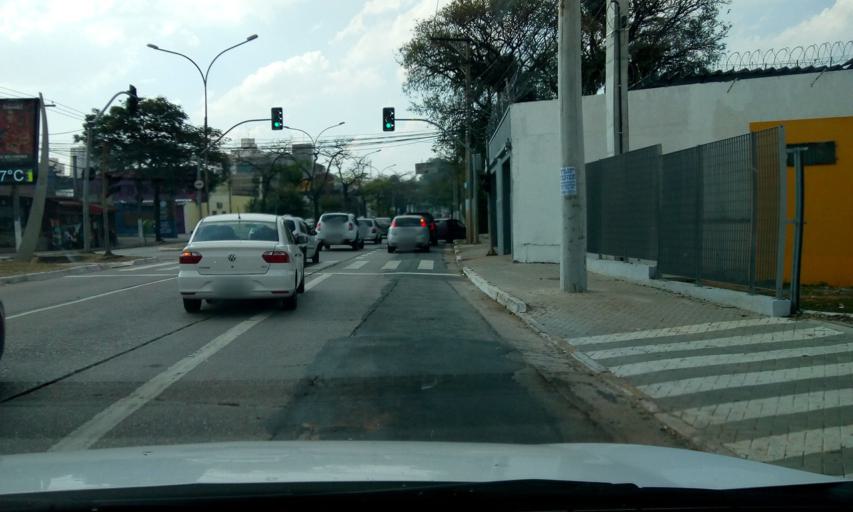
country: BR
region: Sao Paulo
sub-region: Osasco
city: Osasco
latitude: -23.5394
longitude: -46.7278
